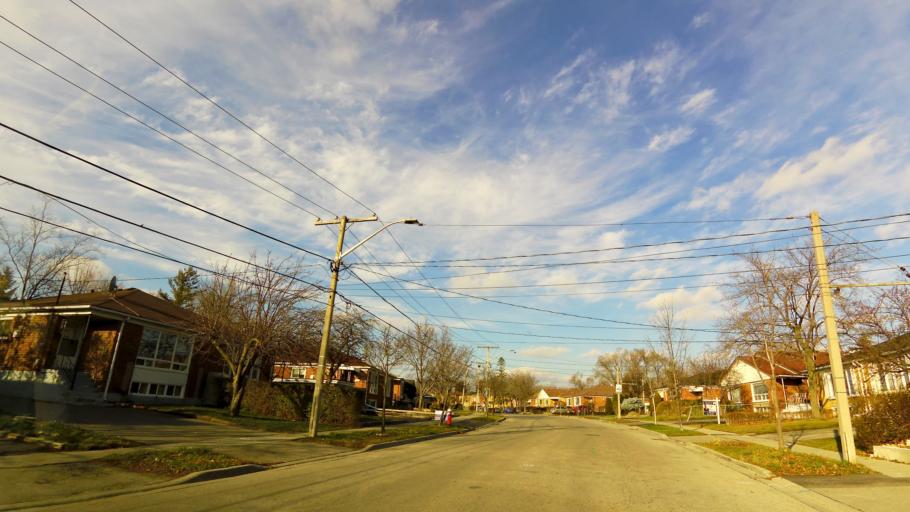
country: CA
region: Ontario
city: Mississauga
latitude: 43.5599
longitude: -79.6612
